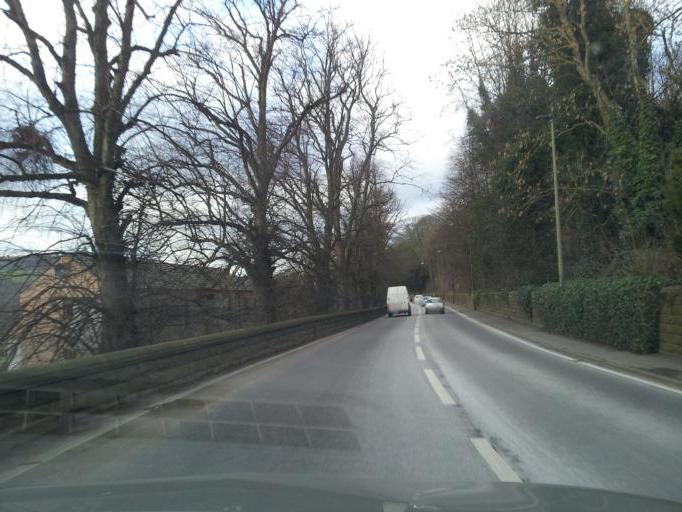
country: GB
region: England
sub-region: Derbyshire
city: Matlock
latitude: 53.1685
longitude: -1.6025
